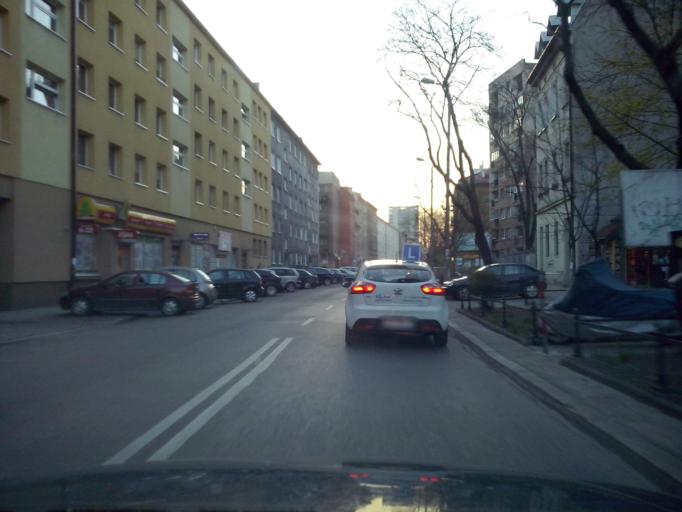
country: PL
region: Lesser Poland Voivodeship
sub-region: Krakow
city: Krakow
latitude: 50.0718
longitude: 19.9240
